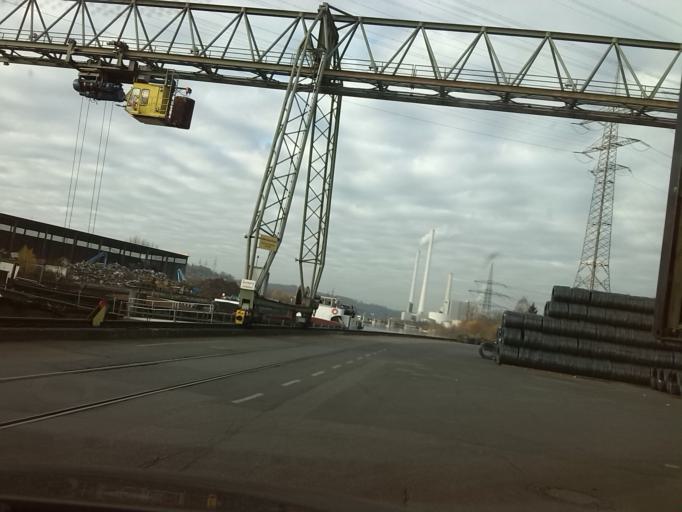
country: DE
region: Baden-Wuerttemberg
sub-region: Regierungsbezirk Stuttgart
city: Deizisau
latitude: 48.7176
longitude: 9.3965
